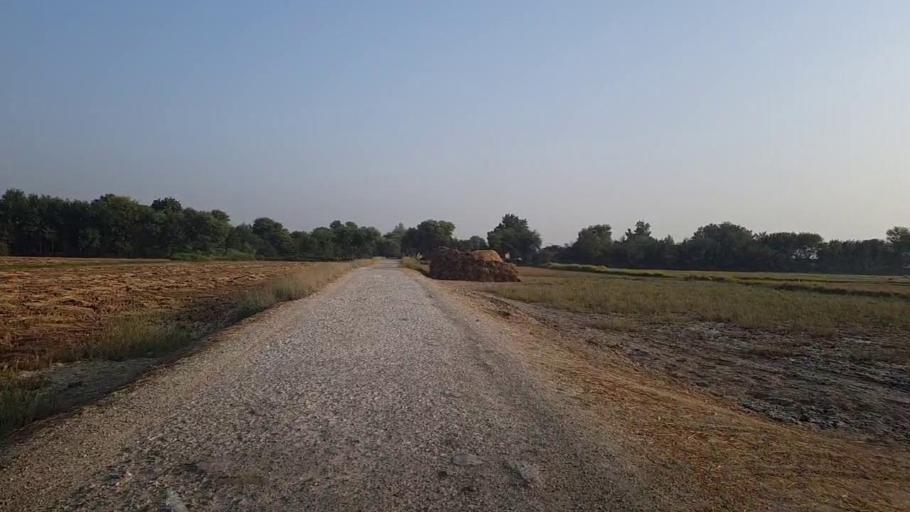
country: PK
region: Sindh
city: Kandhkot
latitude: 28.2426
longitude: 69.0919
